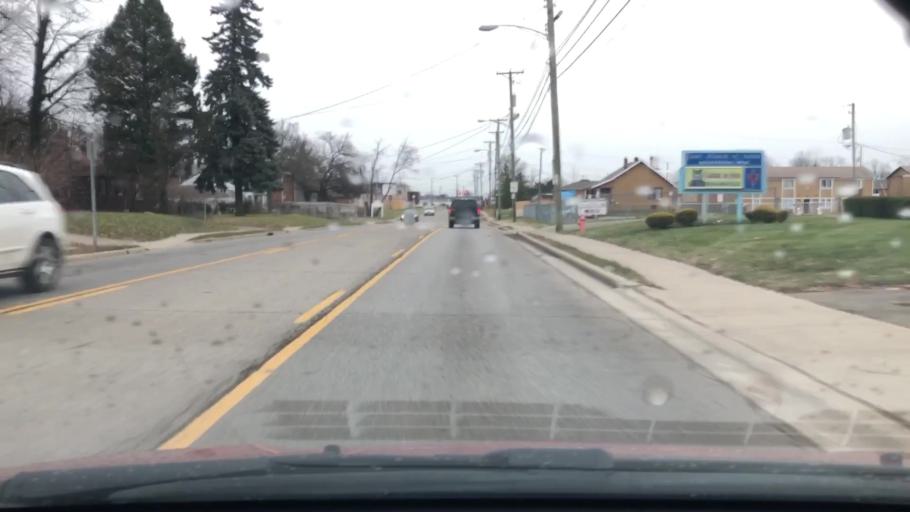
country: US
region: Ohio
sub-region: Franklin County
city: Minerva Park
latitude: 40.0311
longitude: -82.9620
